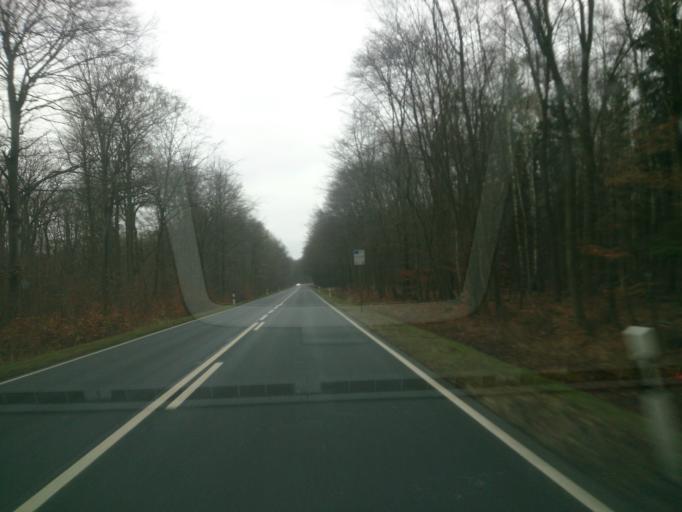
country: DE
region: Mecklenburg-Vorpommern
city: Borrentin
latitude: 53.7515
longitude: 12.9308
